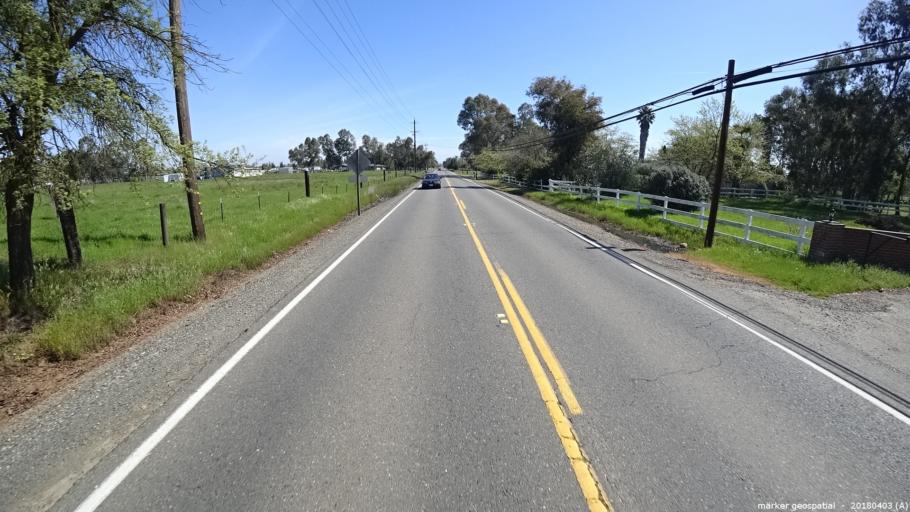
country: US
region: California
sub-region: Sacramento County
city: Wilton
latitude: 38.4109
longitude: -121.2404
